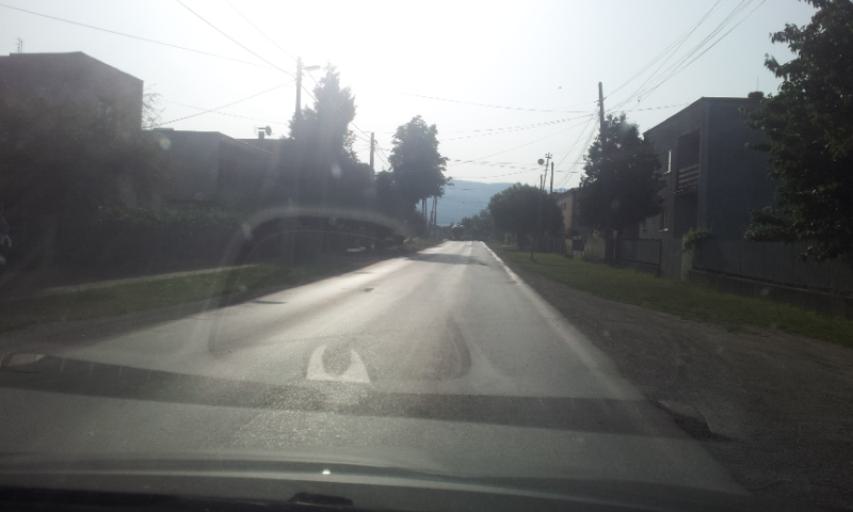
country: SK
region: Kosicky
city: Kosice
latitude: 48.6067
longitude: 21.3145
